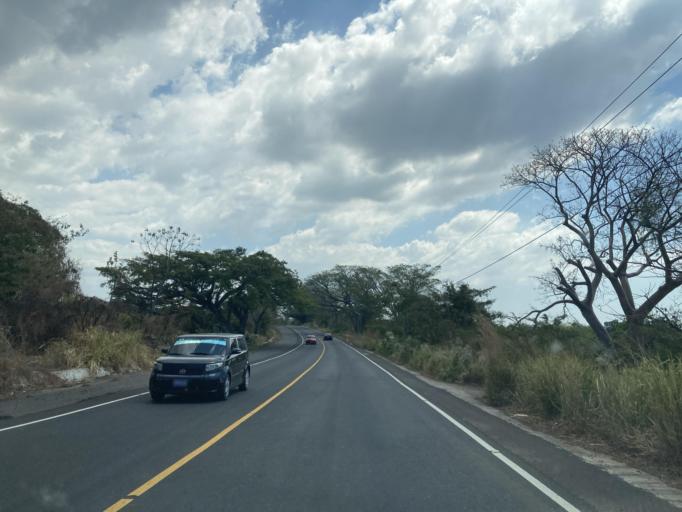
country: GT
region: Santa Rosa
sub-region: Municipio de Taxisco
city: Taxisco
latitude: 14.0944
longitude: -90.5260
